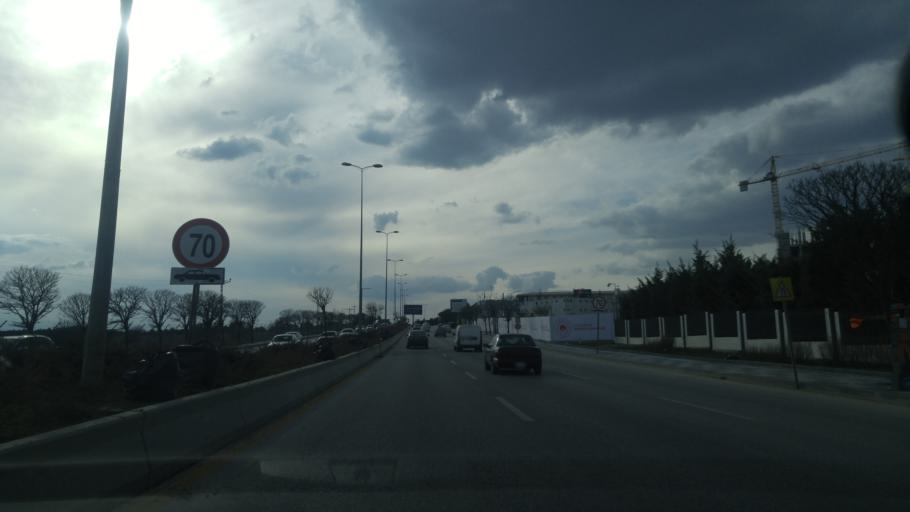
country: TR
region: Ankara
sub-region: Goelbasi
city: Golbasi
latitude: 39.8438
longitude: 32.7873
